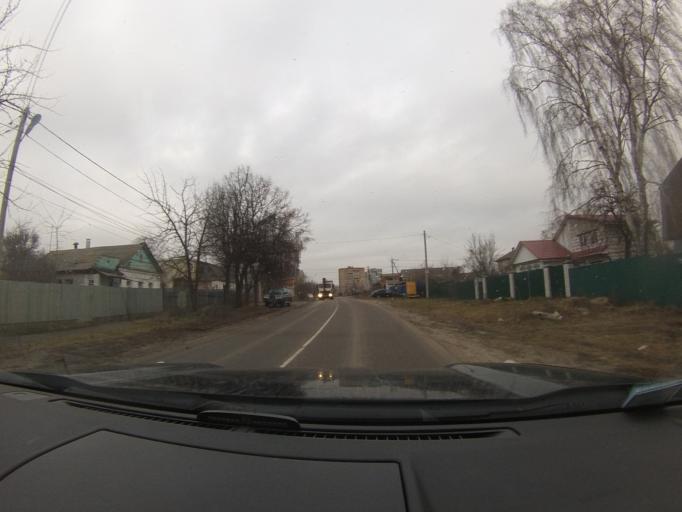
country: RU
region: Moskovskaya
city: Peski
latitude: 55.2670
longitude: 38.7547
